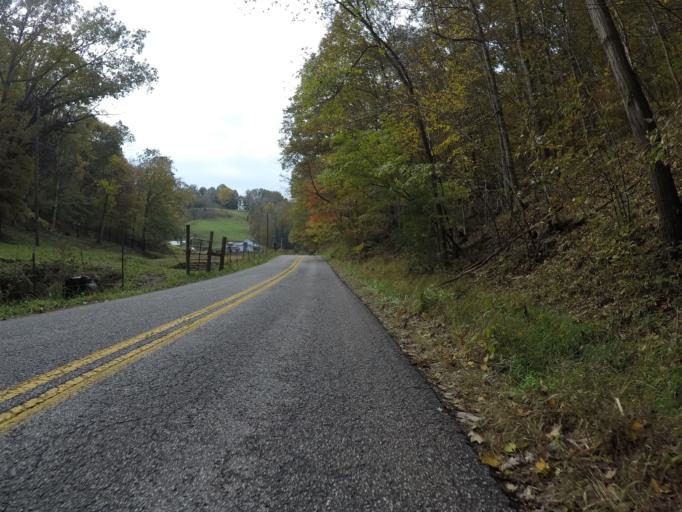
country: US
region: West Virginia
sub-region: Cabell County
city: Huntington
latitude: 38.3718
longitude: -82.4123
